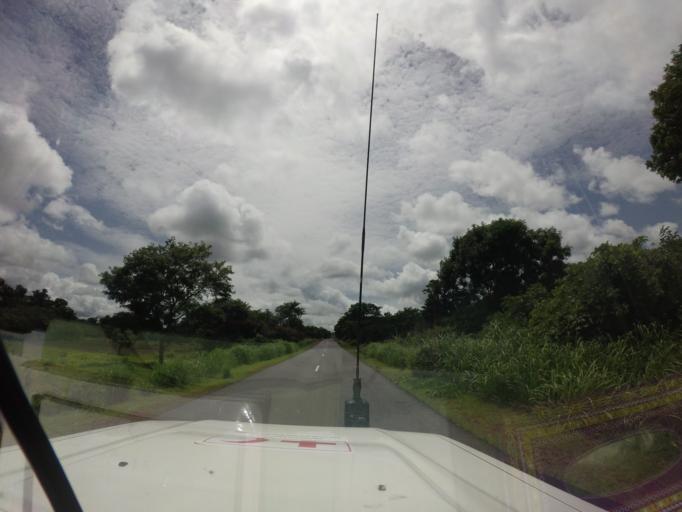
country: SL
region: Northern Province
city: Gberia Fotombu
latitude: 10.1262
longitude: -11.1602
